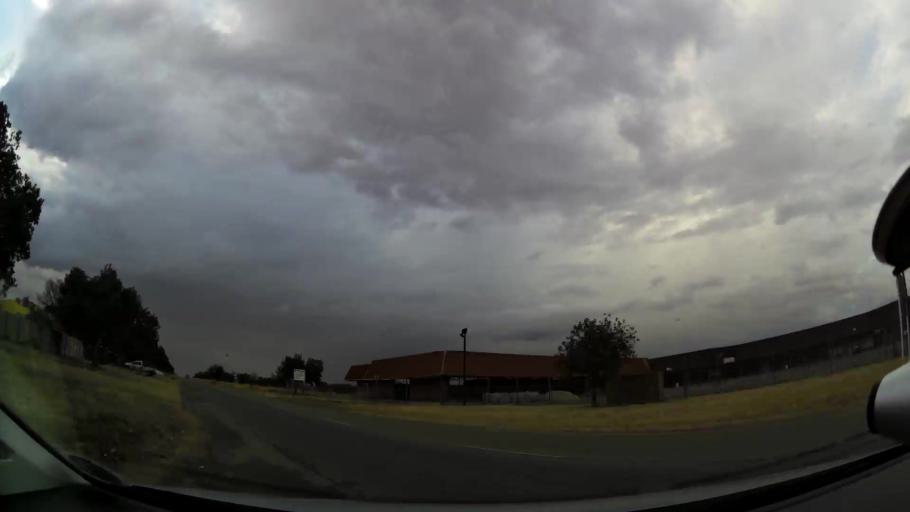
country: ZA
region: Orange Free State
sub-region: Lejweleputswa District Municipality
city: Welkom
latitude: -27.9513
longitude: 26.7349
